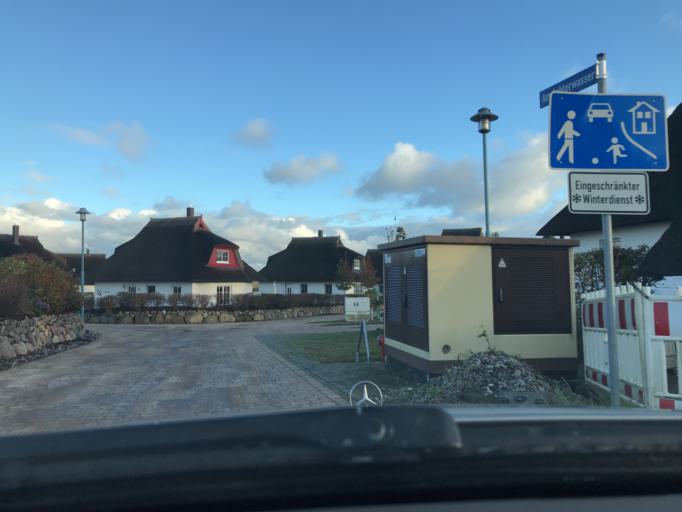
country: DE
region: Mecklenburg-Vorpommern
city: Ostseebad Zinnowitz
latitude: 54.0634
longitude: 13.9057
